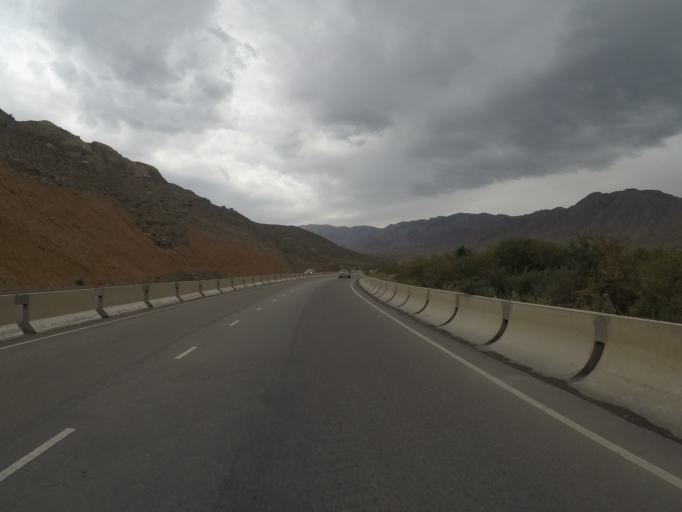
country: KG
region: Naryn
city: Kochkor
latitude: 42.4841
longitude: 75.8662
